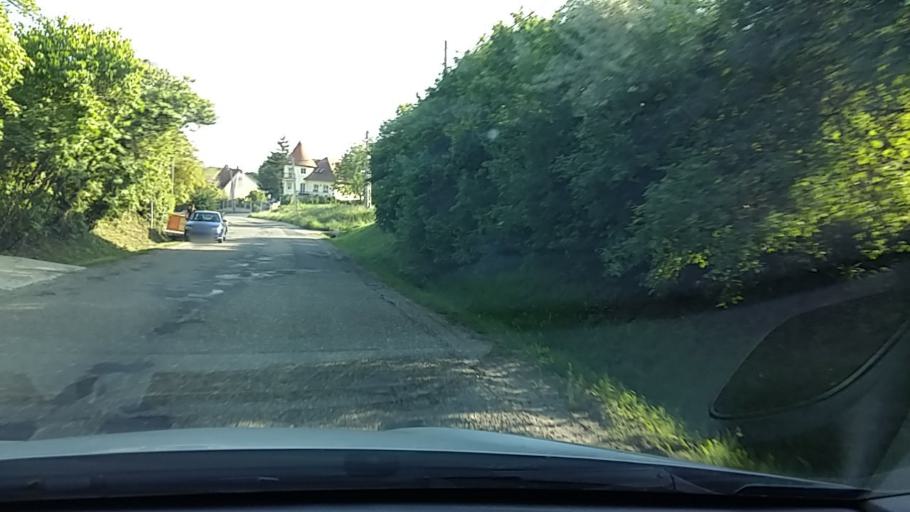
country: HU
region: Pest
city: Kosd
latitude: 47.8113
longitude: 19.2510
